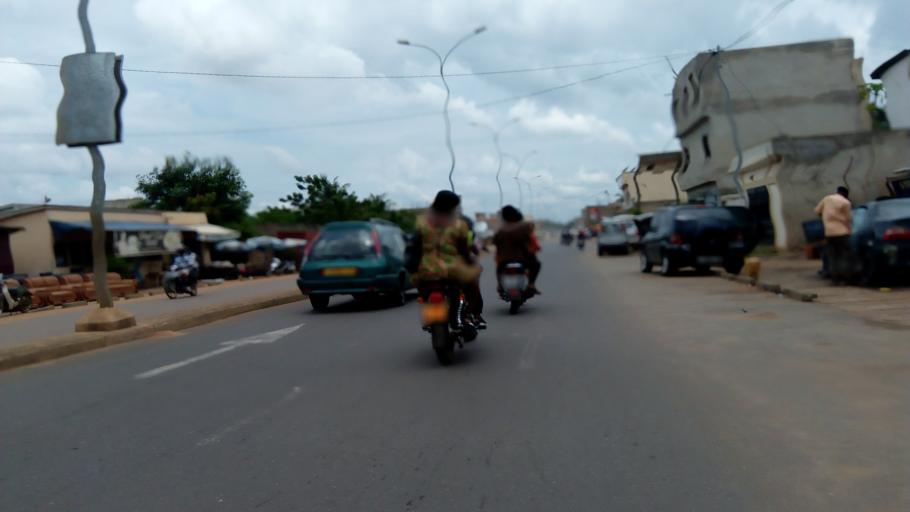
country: TG
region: Maritime
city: Lome
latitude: 6.2147
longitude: 1.1735
